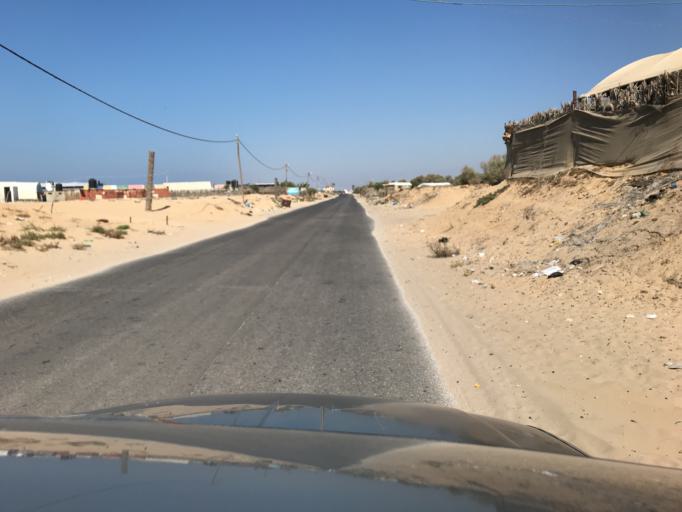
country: PS
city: Wadi as Salqa
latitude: 31.3936
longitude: 34.3006
